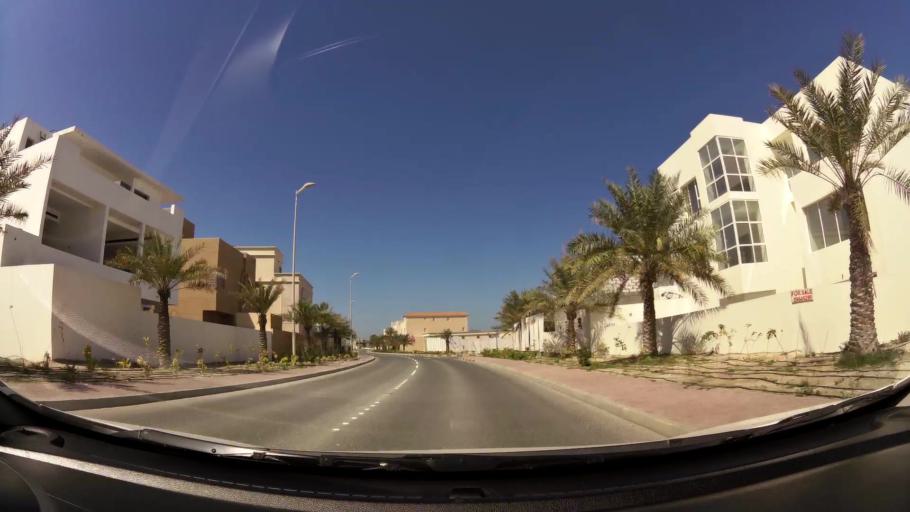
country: BH
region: Muharraq
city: Al Hadd
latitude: 26.2904
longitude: 50.6745
